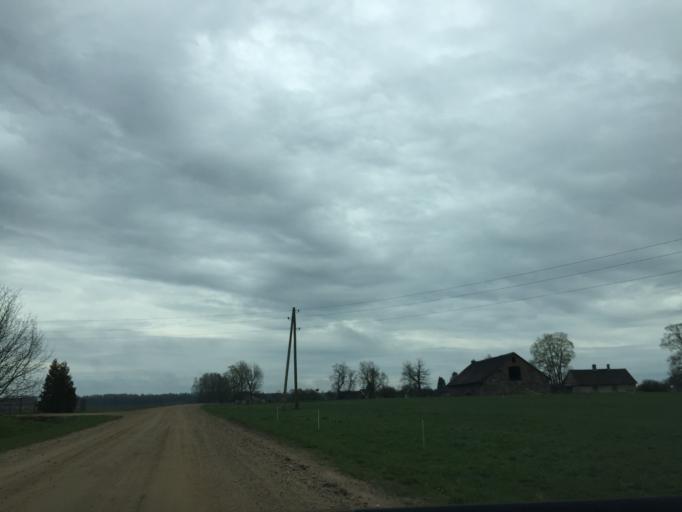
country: LV
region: Sigulda
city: Sigulda
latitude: 57.0438
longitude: 24.8399
